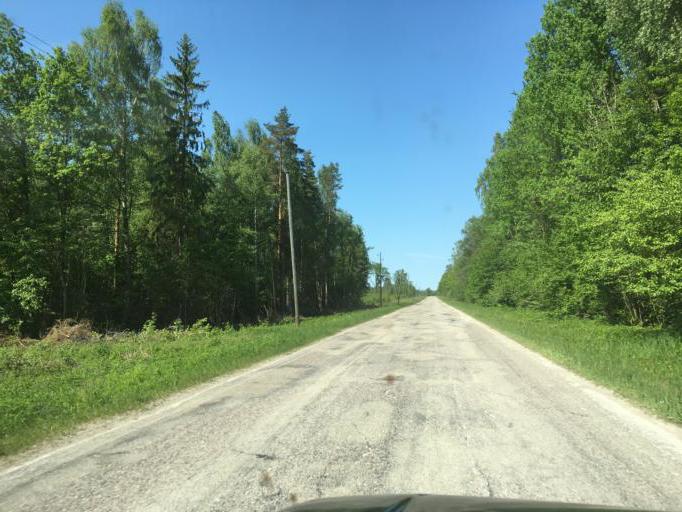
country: LV
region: Dundaga
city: Dundaga
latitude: 57.4551
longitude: 22.3214
